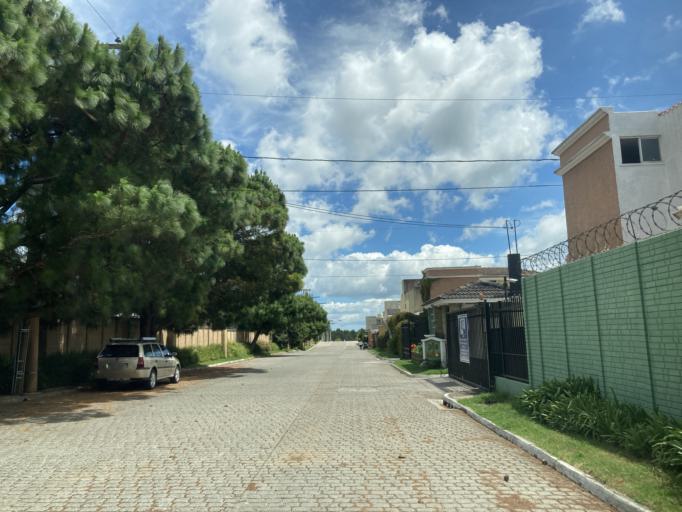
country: GT
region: Guatemala
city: San Jose Pinula
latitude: 14.5395
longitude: -90.4355
